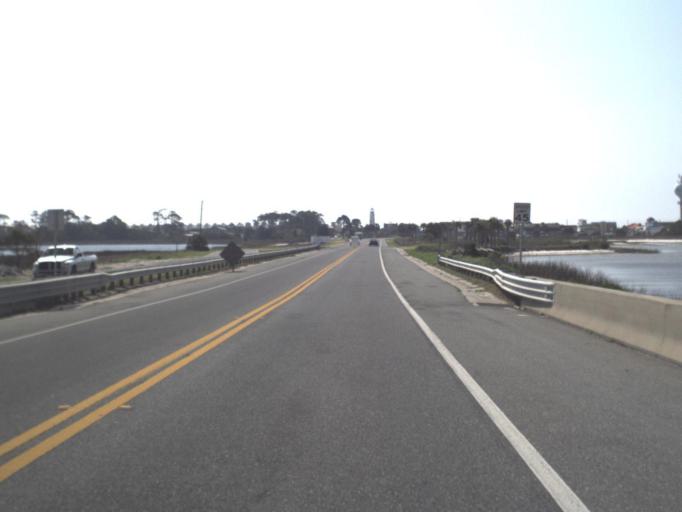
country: US
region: Florida
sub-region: Franklin County
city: Eastpoint
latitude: 29.6698
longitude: -84.8667
